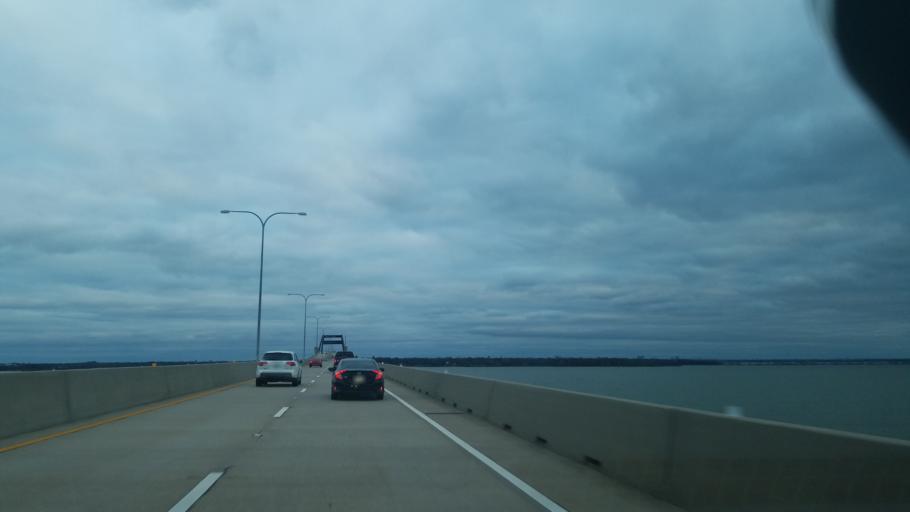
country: US
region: Texas
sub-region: Denton County
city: Lake Dallas
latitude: 33.1391
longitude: -97.0102
